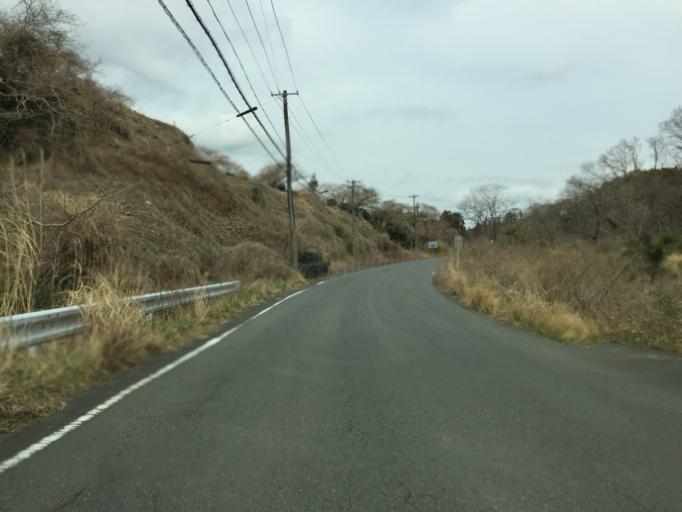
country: JP
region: Fukushima
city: Iwaki
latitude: 37.0030
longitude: 140.8172
